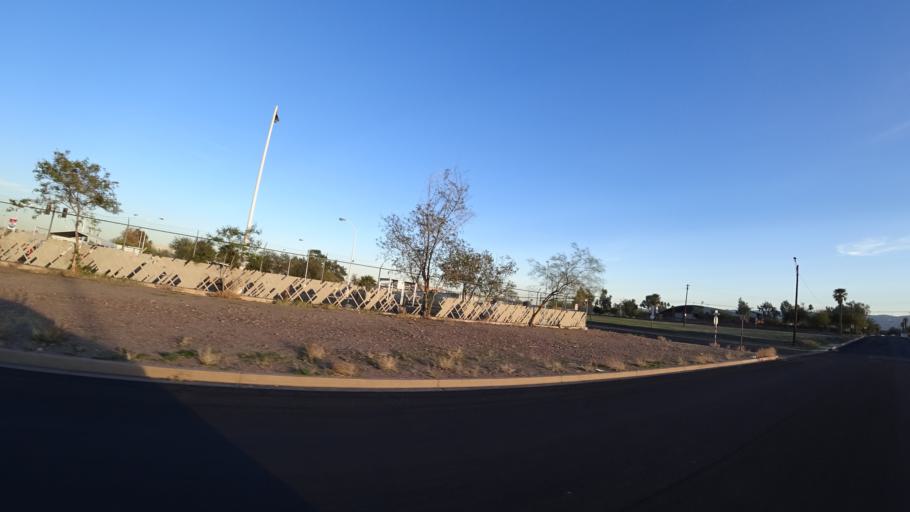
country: US
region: Arizona
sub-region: Maricopa County
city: Phoenix
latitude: 33.4336
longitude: -112.0522
